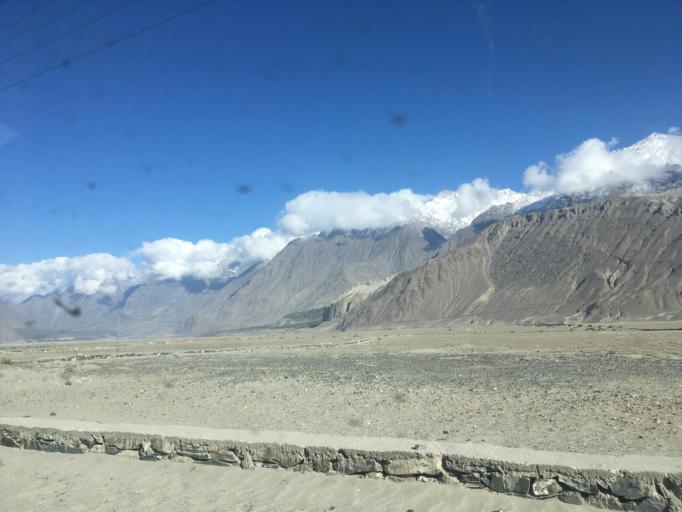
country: PK
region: Gilgit-Baltistan
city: Skardu
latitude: 35.3585
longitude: 75.5382
